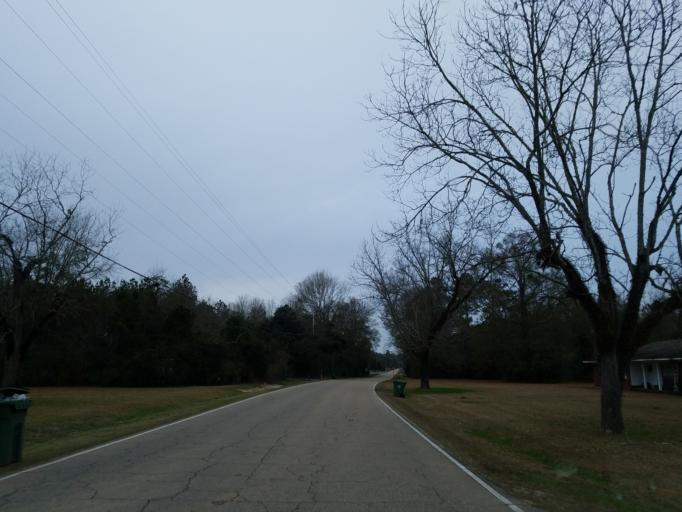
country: US
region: Mississippi
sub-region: Forrest County
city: Hattiesburg
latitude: 31.2868
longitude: -89.2605
